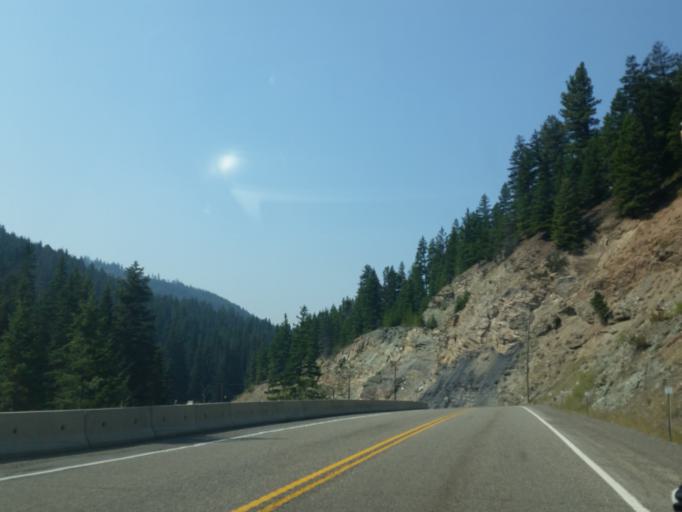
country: CA
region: British Columbia
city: Princeton
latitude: 49.1561
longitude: -120.5854
